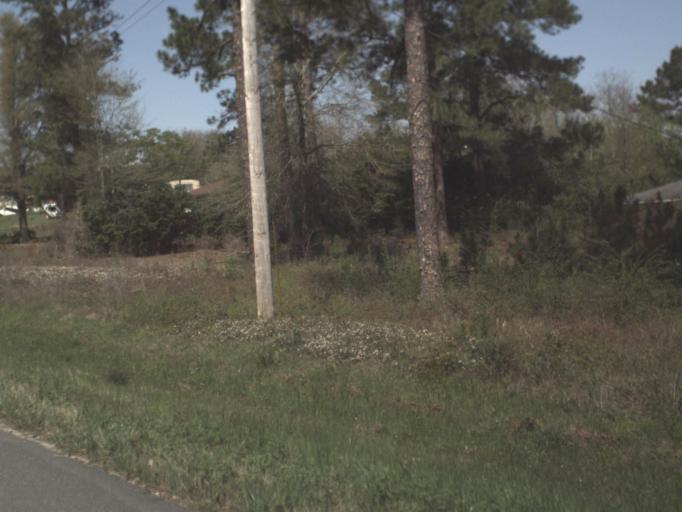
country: US
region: Florida
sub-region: Jackson County
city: Graceville
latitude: 30.9628
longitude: -85.5616
